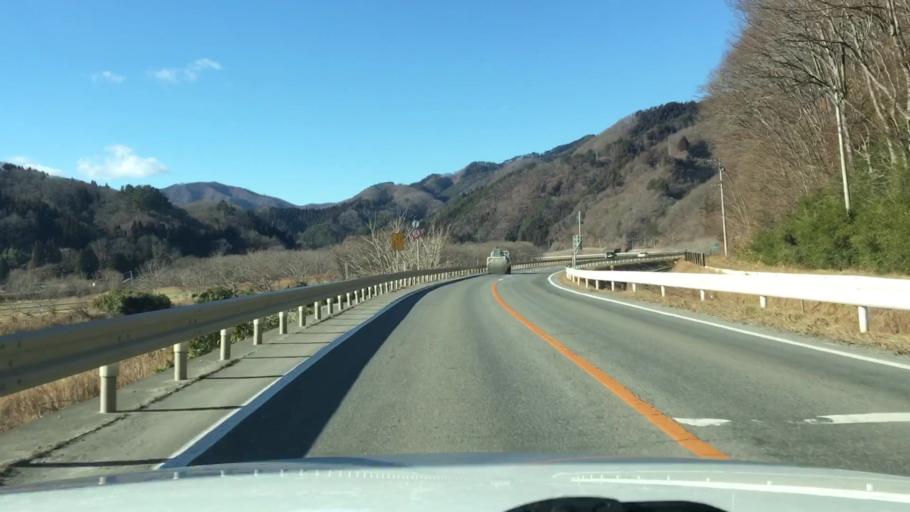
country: JP
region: Iwate
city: Miyako
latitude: 39.6300
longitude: 141.8553
